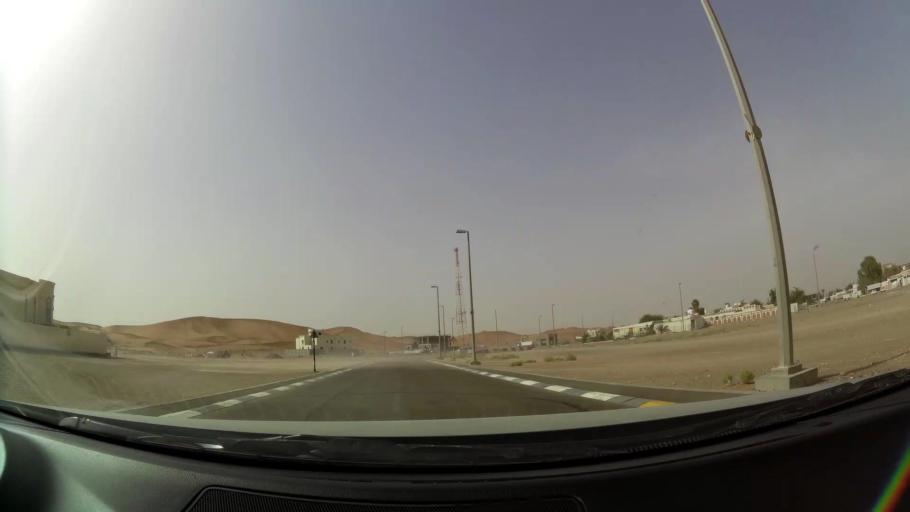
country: AE
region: Abu Dhabi
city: Al Ain
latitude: 24.2081
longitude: 55.5777
